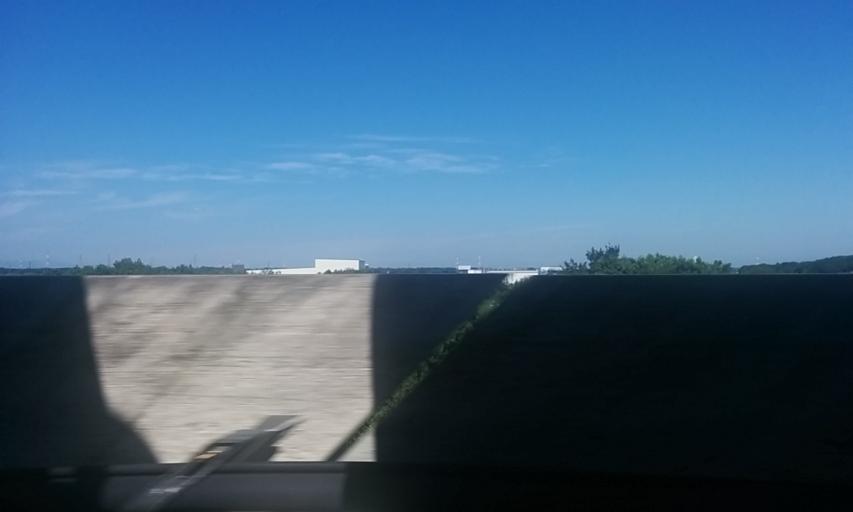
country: JP
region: Ibaraki
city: Moriya
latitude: 35.9337
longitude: 139.9677
